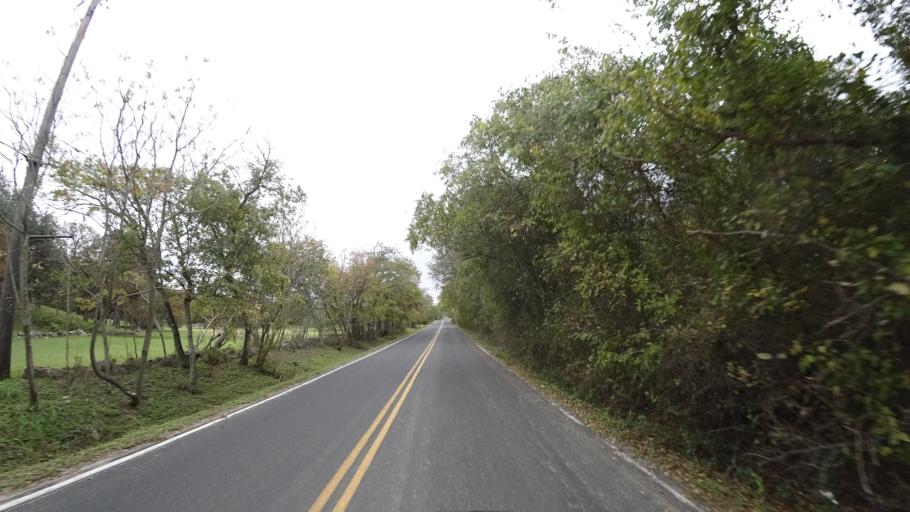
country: US
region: Texas
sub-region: Travis County
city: Manchaca
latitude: 30.1459
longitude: -97.8470
